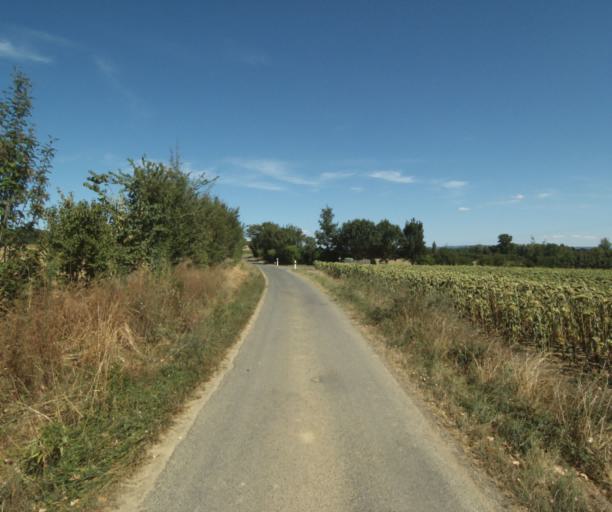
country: FR
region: Midi-Pyrenees
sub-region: Departement de la Haute-Garonne
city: Auriac-sur-Vendinelle
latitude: 43.5184
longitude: 1.8958
